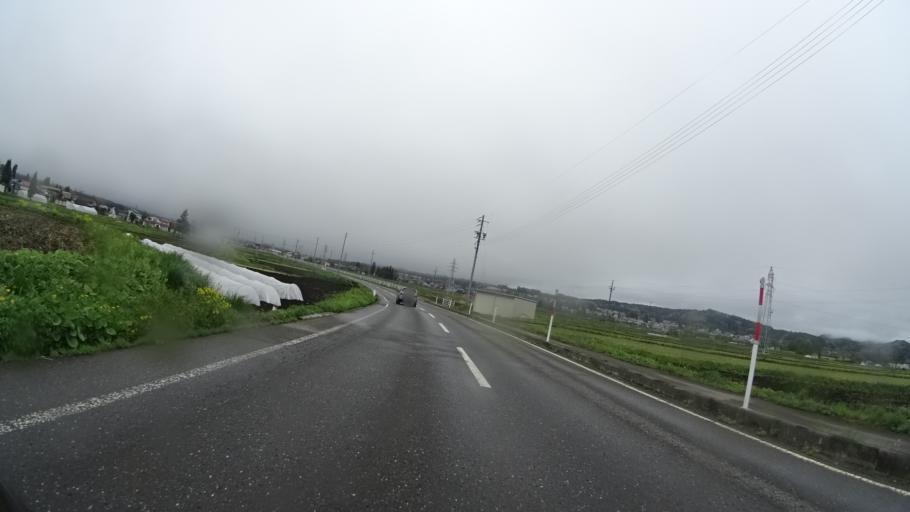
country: JP
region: Nagano
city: Nagano-shi
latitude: 36.7969
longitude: 138.1959
